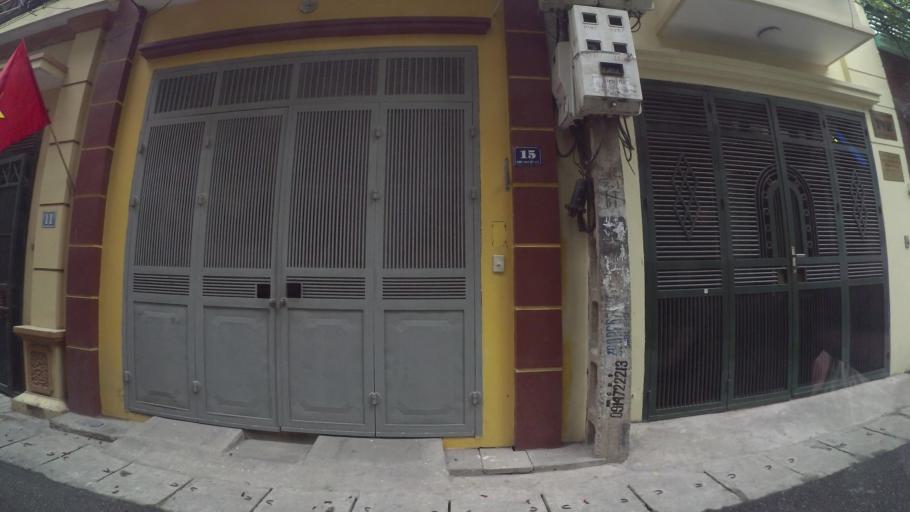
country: VN
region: Ha Noi
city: Hai BaTrung
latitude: 21.0015
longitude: 105.8640
